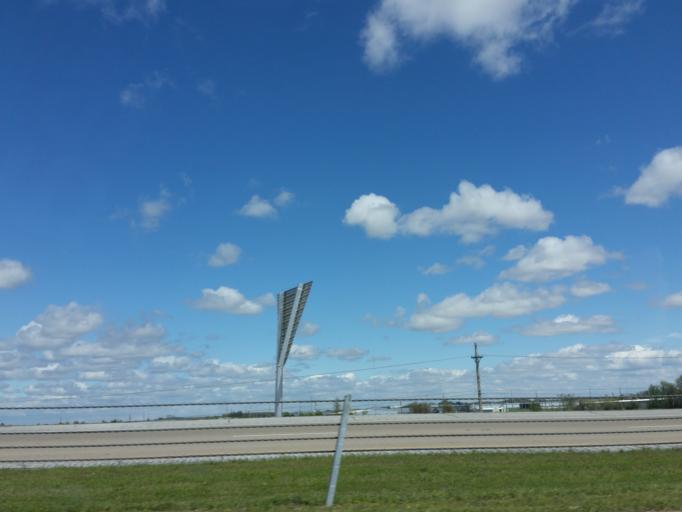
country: US
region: Arkansas
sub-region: Craighead County
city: Jonesboro
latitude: 35.8066
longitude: -90.6329
